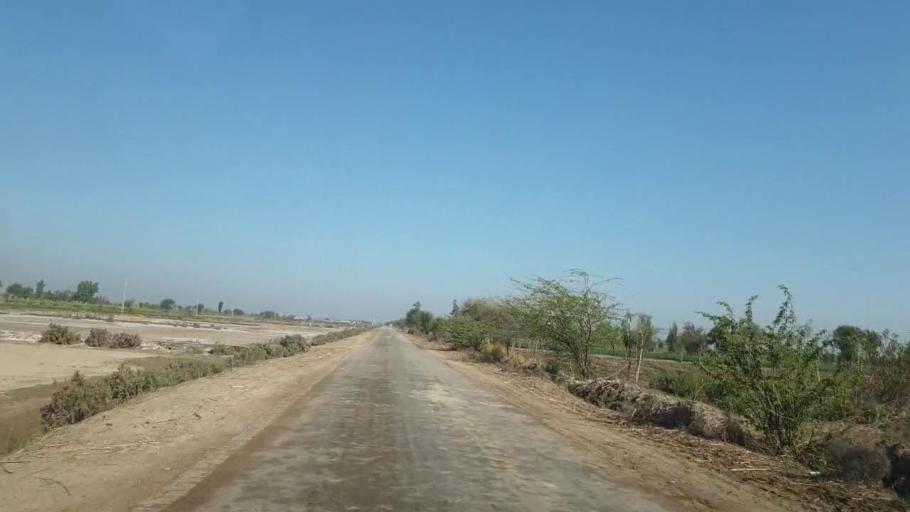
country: PK
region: Sindh
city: Mirpur Khas
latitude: 25.5850
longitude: 69.0456
